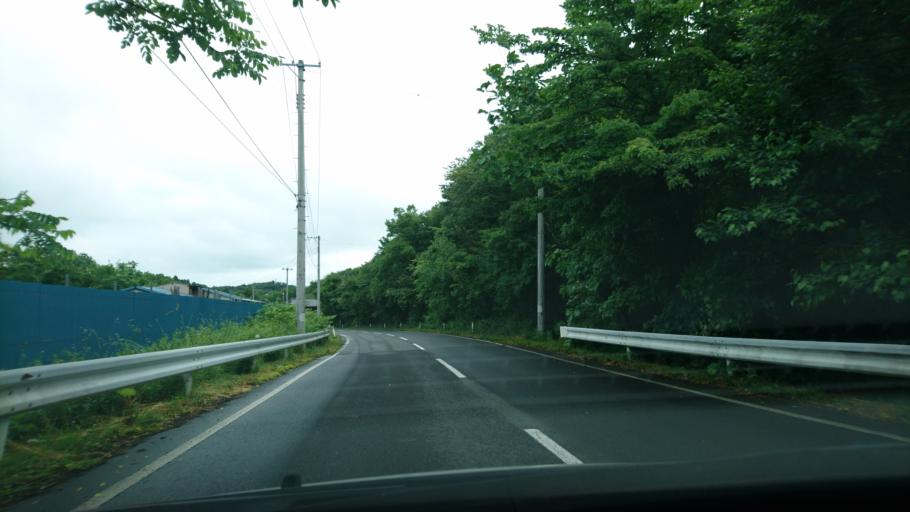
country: JP
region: Iwate
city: Ichinoseki
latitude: 38.8928
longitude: 141.1523
